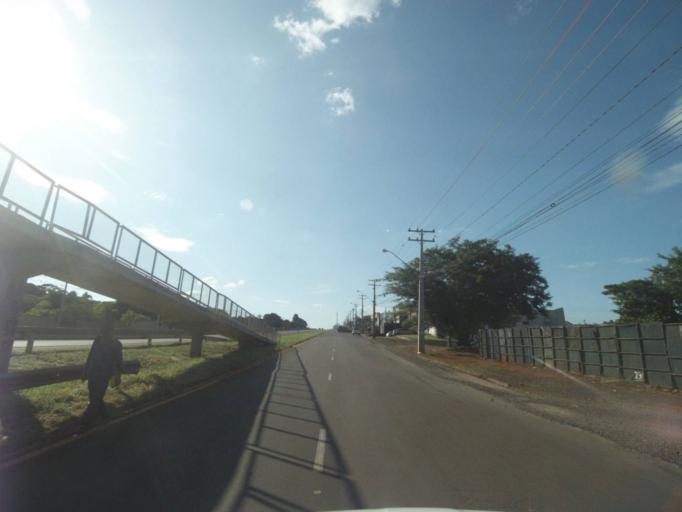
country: BR
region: Parana
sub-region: Londrina
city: Londrina
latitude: -23.3538
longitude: -51.1615
